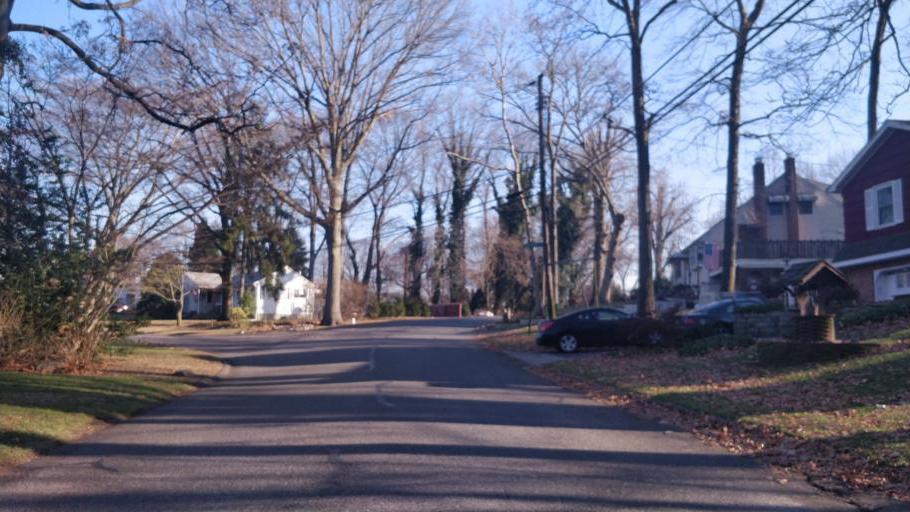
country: US
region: New York
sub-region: Nassau County
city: Bayville
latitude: 40.9067
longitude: -73.5774
